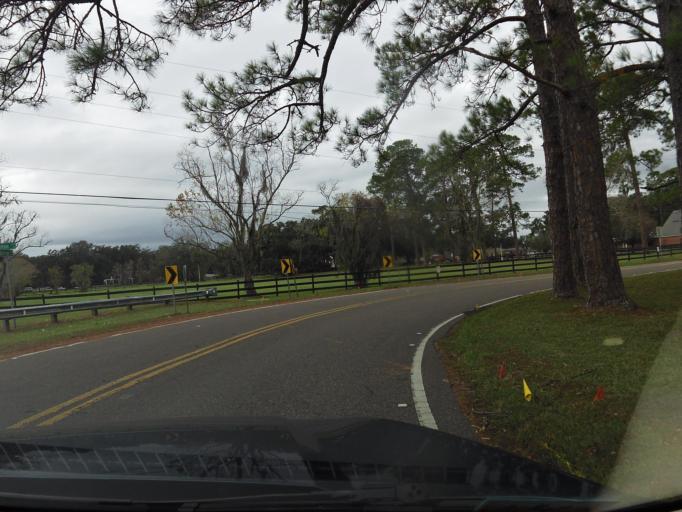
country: US
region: Florida
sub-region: Duval County
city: Jacksonville
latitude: 30.3005
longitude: -81.6028
